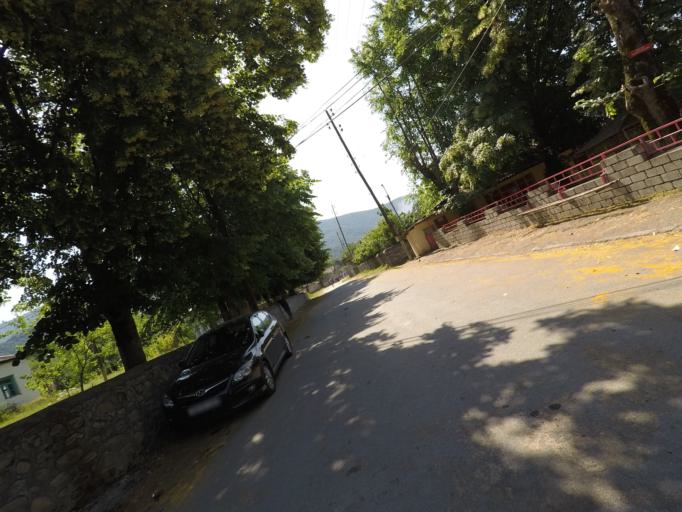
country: AZ
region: Qakh Rayon
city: Cinarli
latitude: 41.4845
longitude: 46.8446
